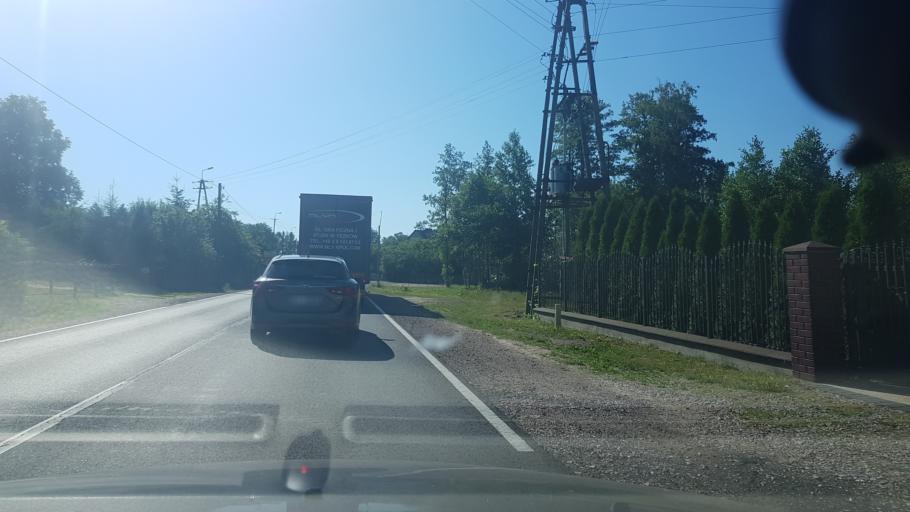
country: PL
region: Masovian Voivodeship
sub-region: Powiat wegrowski
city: Lochow
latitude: 52.5442
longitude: 21.6413
